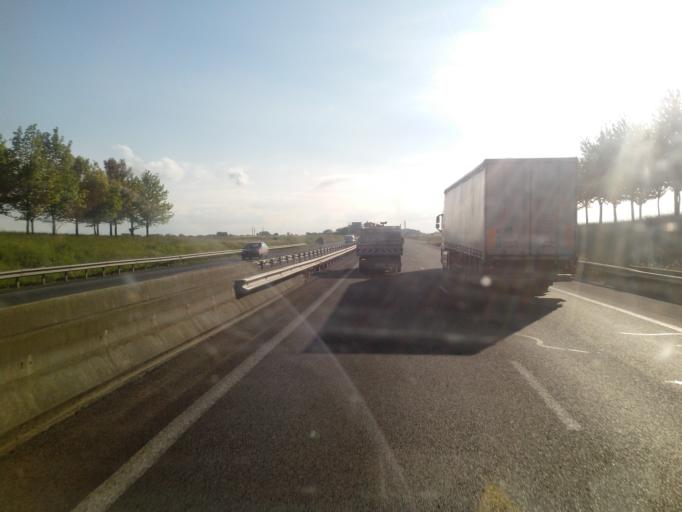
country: FR
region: Lower Normandy
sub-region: Departement du Calvados
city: Verson
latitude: 49.1589
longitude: -0.4683
